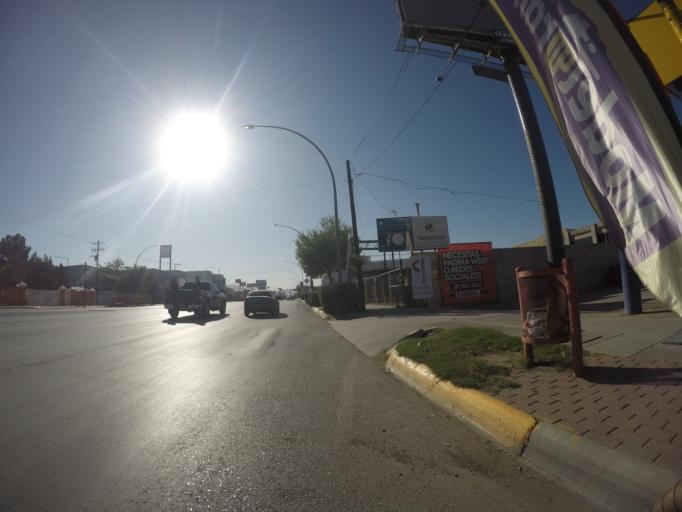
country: MX
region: Chihuahua
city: Ciudad Juarez
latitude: 31.7384
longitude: -106.4358
